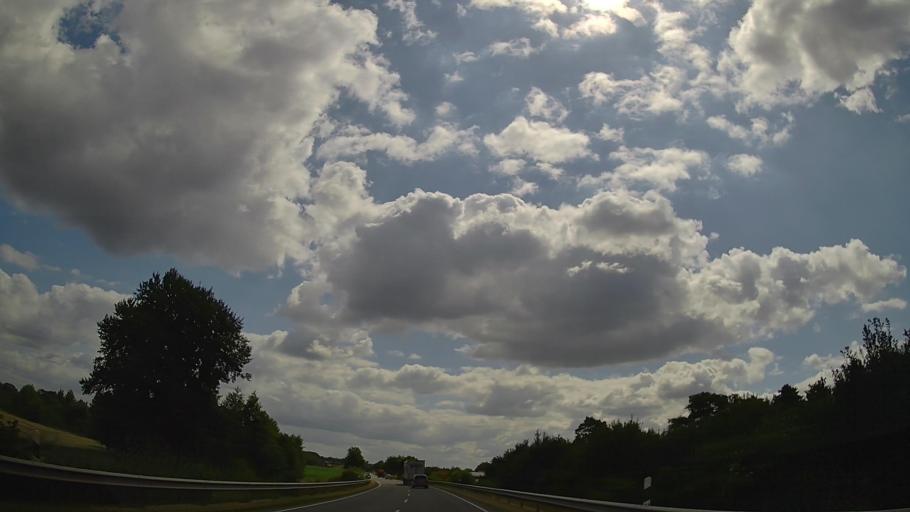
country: DE
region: Lower Saxony
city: Vechta
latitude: 52.7050
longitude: 8.2697
